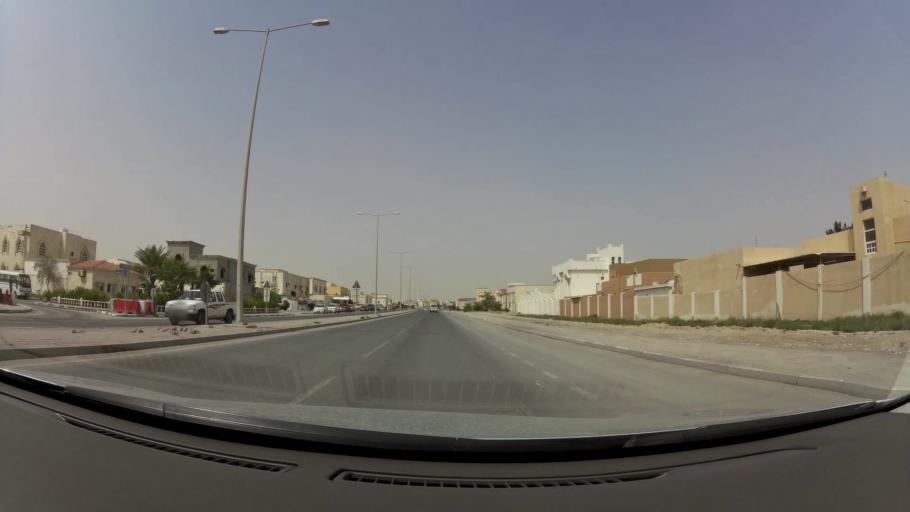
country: QA
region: Baladiyat ar Rayyan
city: Ar Rayyan
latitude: 25.2415
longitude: 51.4204
